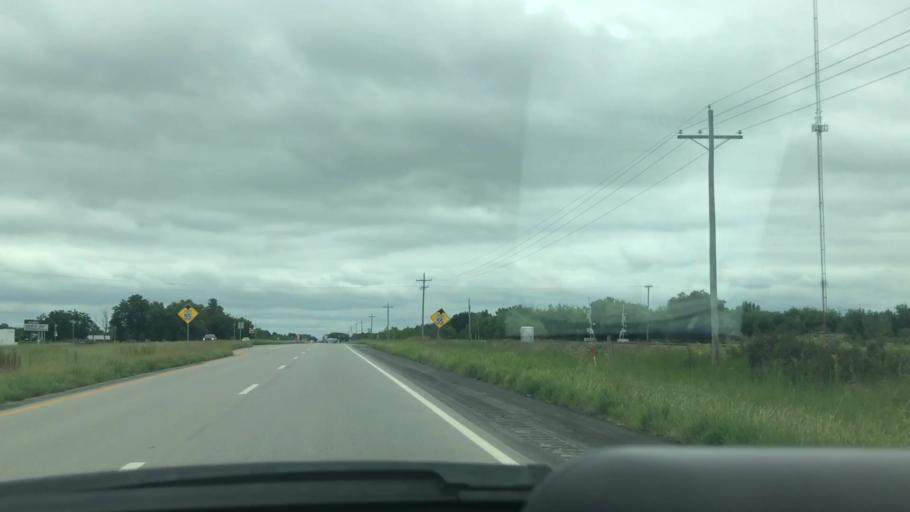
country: US
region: Oklahoma
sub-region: Mayes County
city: Pryor
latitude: 36.4224
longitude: -95.2769
